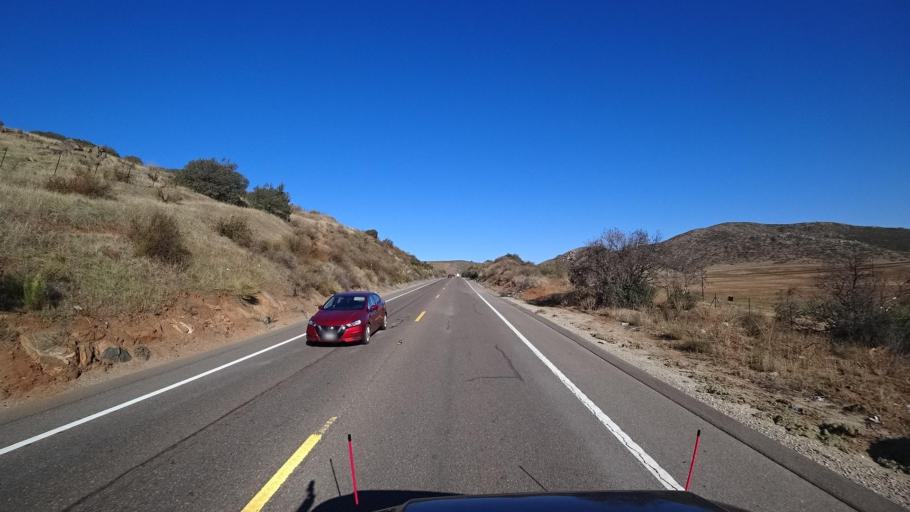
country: US
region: California
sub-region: San Diego County
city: Jamul
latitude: 32.6747
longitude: -116.8365
